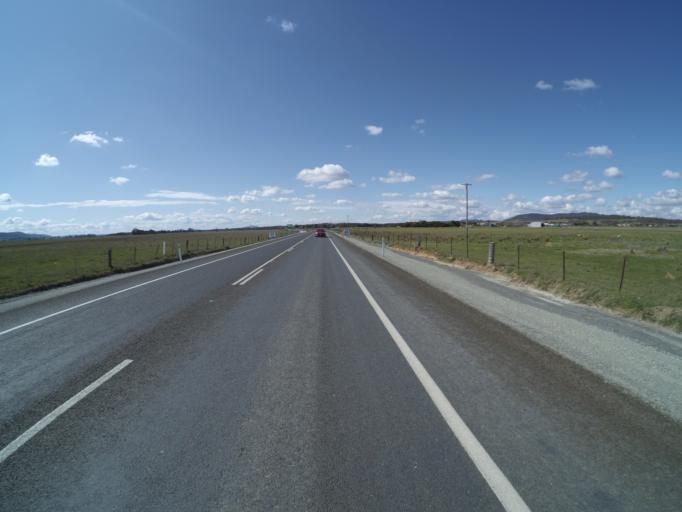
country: AU
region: New South Wales
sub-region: Palerang
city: Bungendore
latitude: -35.2711
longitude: 149.4289
